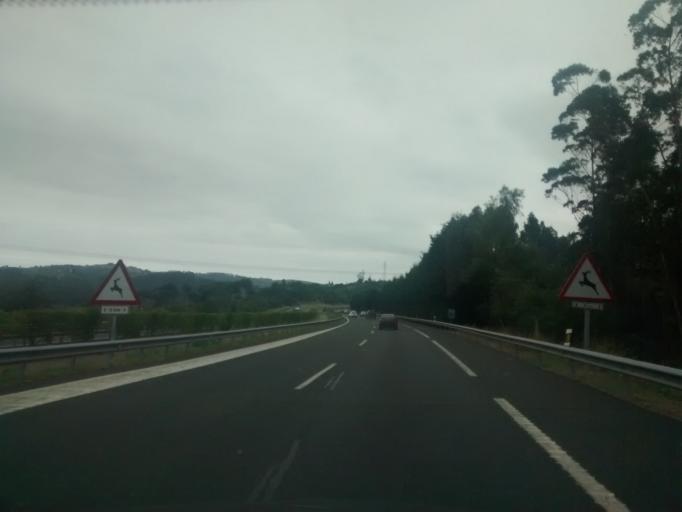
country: ES
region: Cantabria
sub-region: Provincia de Cantabria
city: Luzmela
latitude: 43.3308
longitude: -4.1600
